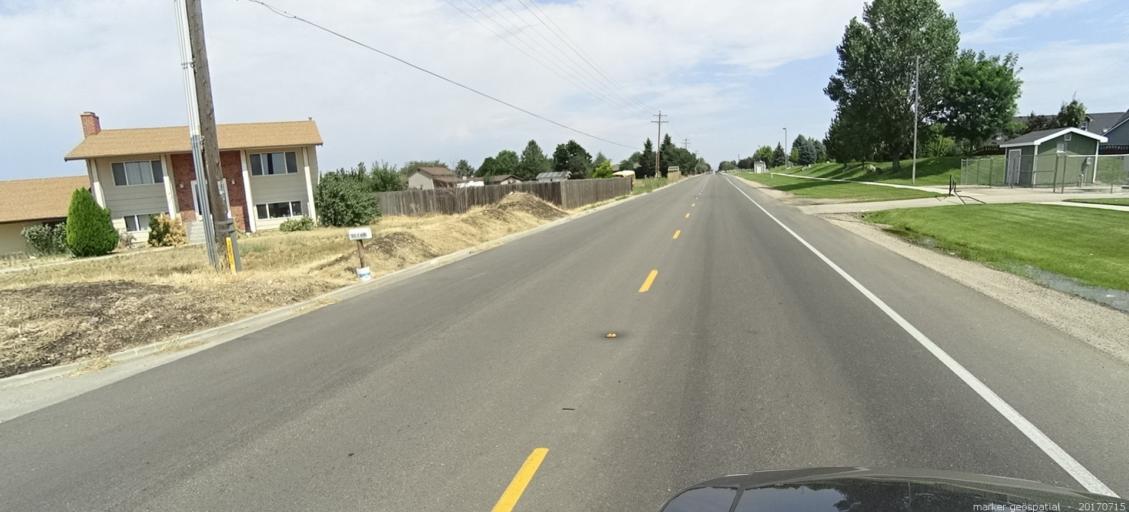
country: US
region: Idaho
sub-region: Ada County
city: Garden City
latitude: 43.5465
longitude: -116.2742
